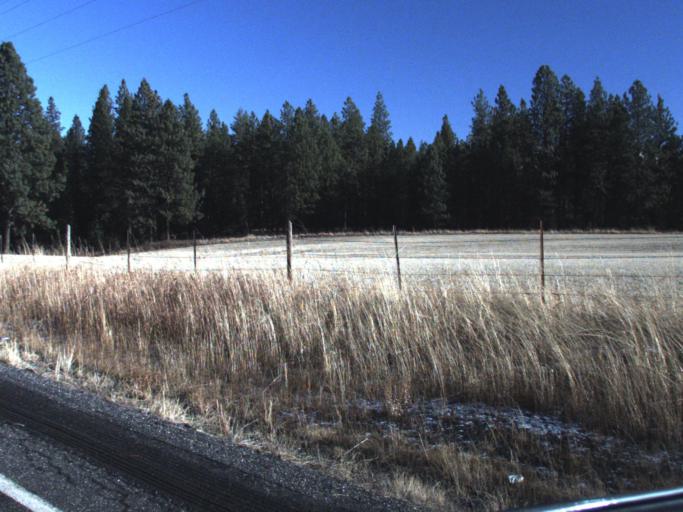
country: US
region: Washington
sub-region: Asotin County
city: Asotin
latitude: 46.0954
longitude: -117.1524
